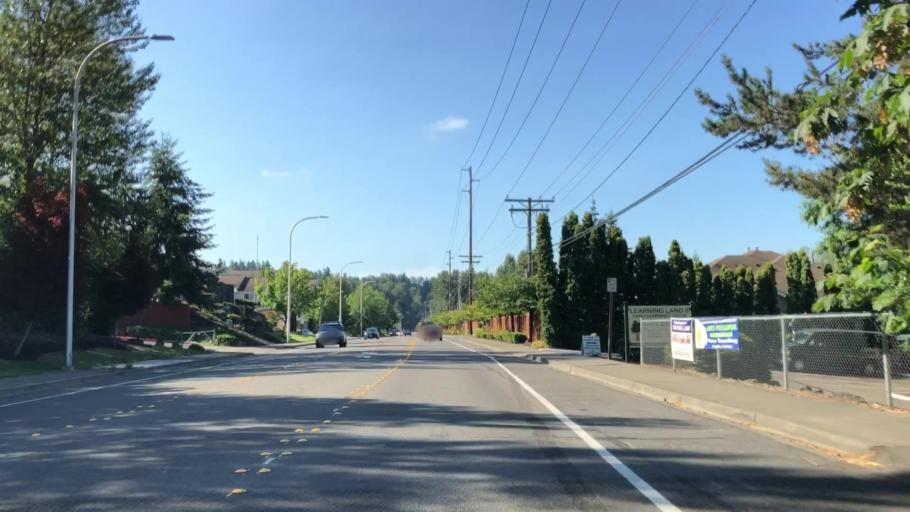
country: US
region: Washington
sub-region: King County
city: East Hill-Meridian
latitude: 47.4357
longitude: -122.2131
